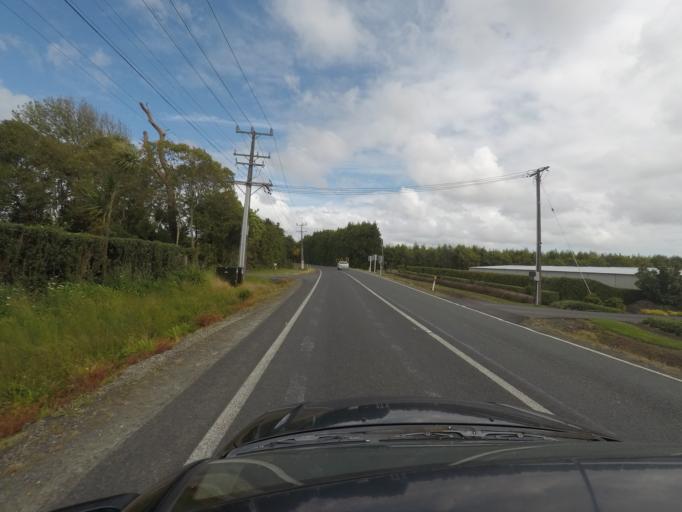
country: NZ
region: Auckland
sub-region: Auckland
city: Muriwai Beach
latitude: -36.7726
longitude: 174.5737
